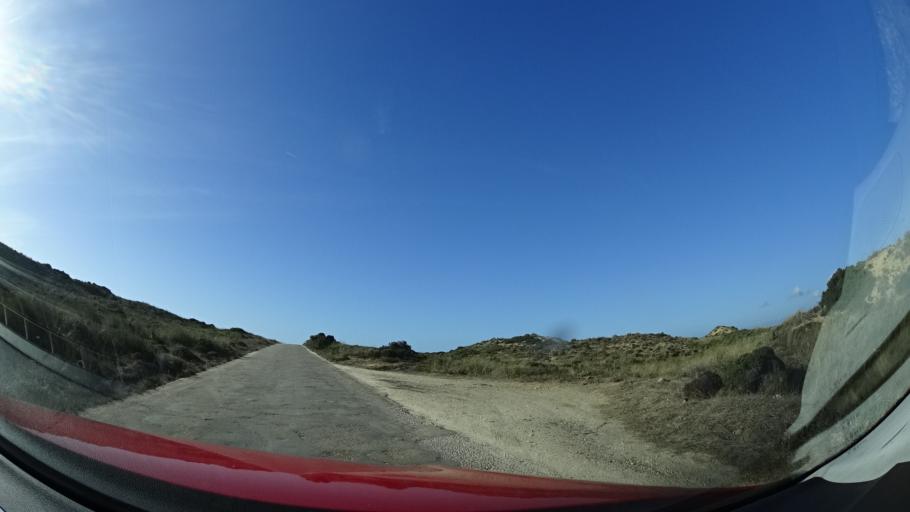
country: PT
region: Faro
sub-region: Vila do Bispo
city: Vila do Bispo
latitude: 37.1941
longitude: -8.9059
